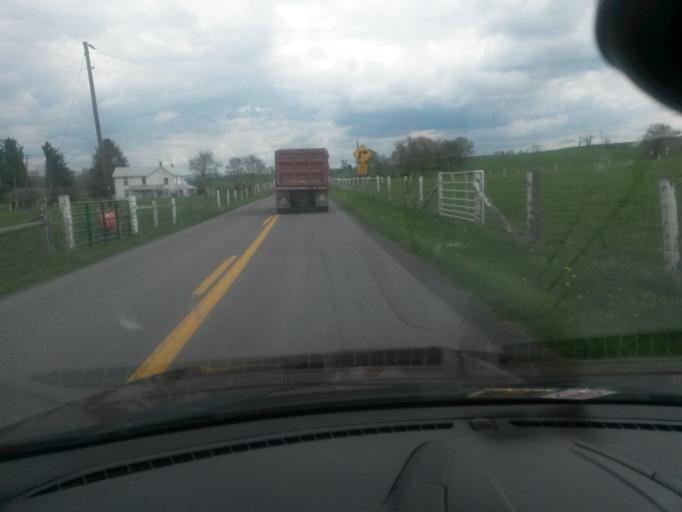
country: US
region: West Virginia
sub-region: Greenbrier County
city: Lewisburg
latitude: 37.8963
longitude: -80.4134
